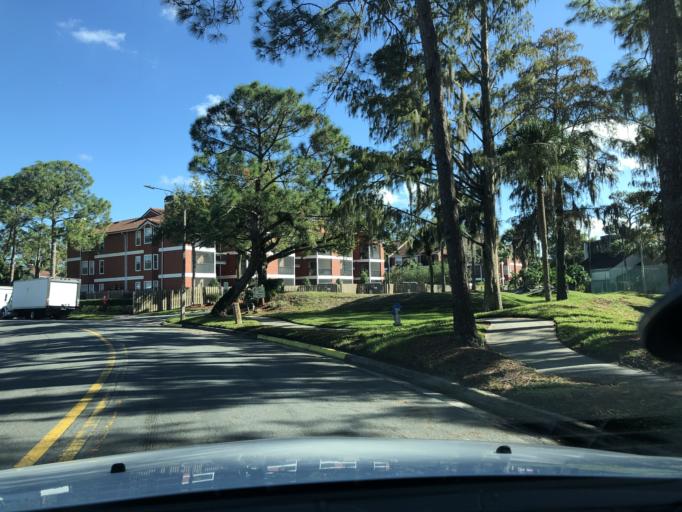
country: US
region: Florida
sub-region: Orange County
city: Oak Ridge
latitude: 28.4921
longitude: -81.4520
